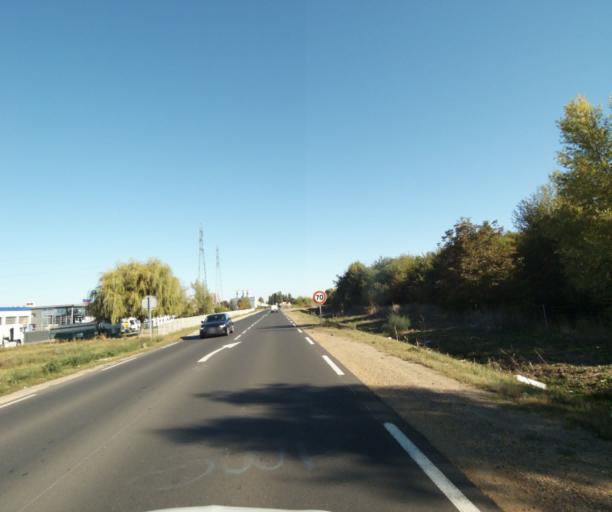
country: FR
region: Auvergne
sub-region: Departement du Puy-de-Dome
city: Gerzat
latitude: 45.8089
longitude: 3.1513
